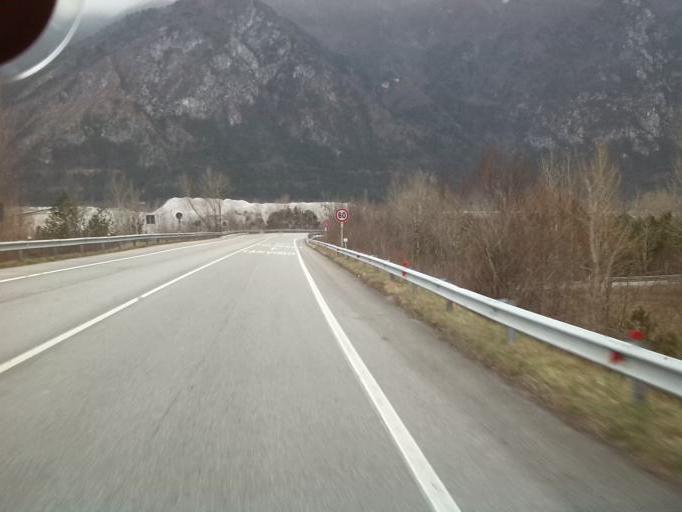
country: IT
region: Friuli Venezia Giulia
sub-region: Provincia di Udine
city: Amaro
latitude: 46.3791
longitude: 13.1336
